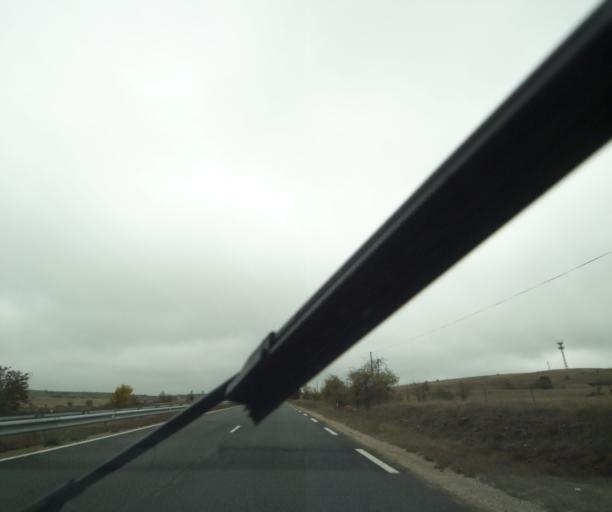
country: FR
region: Midi-Pyrenees
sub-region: Departement de l'Aveyron
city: La Cavalerie
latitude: 44.0434
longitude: 3.1403
